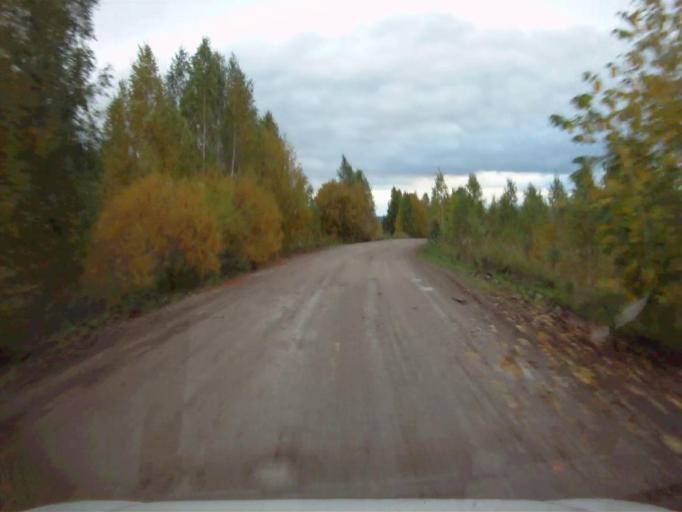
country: RU
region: Sverdlovsk
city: Mikhaylovsk
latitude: 56.2012
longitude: 59.2005
